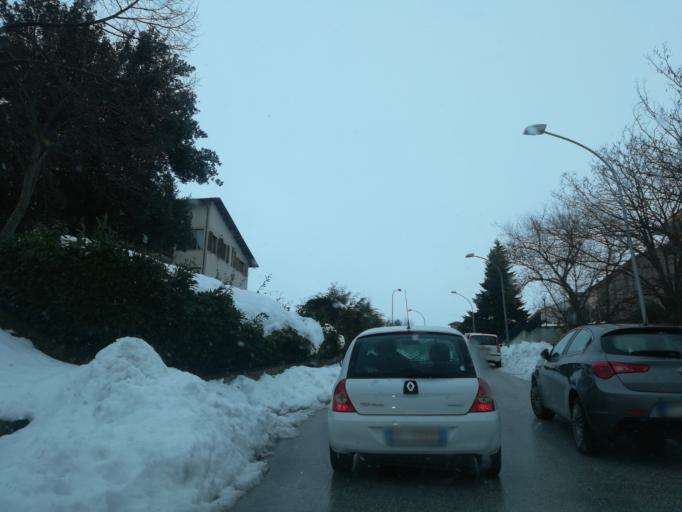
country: IT
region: Molise
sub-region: Provincia di Isernia
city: Agnone
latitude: 41.8094
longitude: 14.3771
